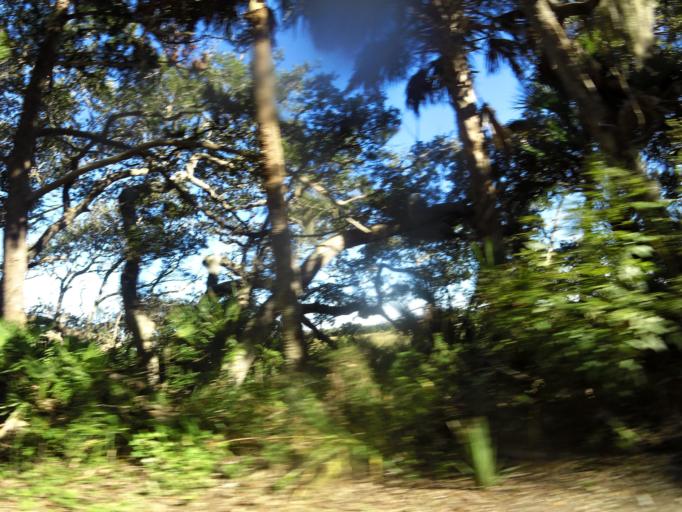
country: US
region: Florida
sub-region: Duval County
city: Atlantic Beach
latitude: 30.4131
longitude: -81.4294
